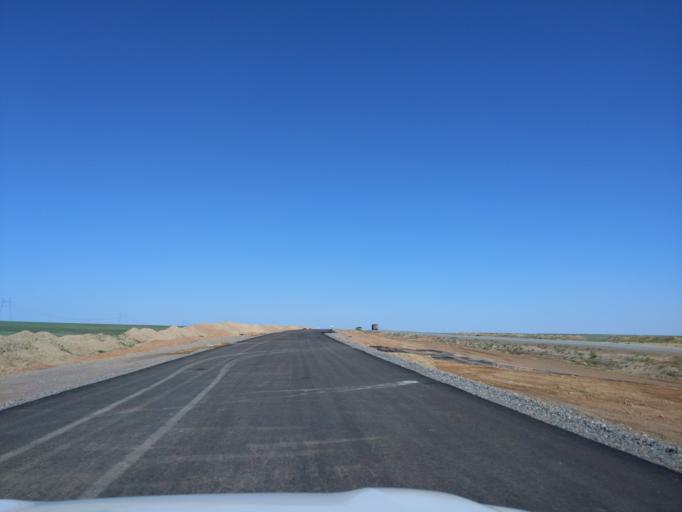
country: KZ
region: Almaty Oblysy
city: Bakanas
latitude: 44.0316
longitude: 76.0917
